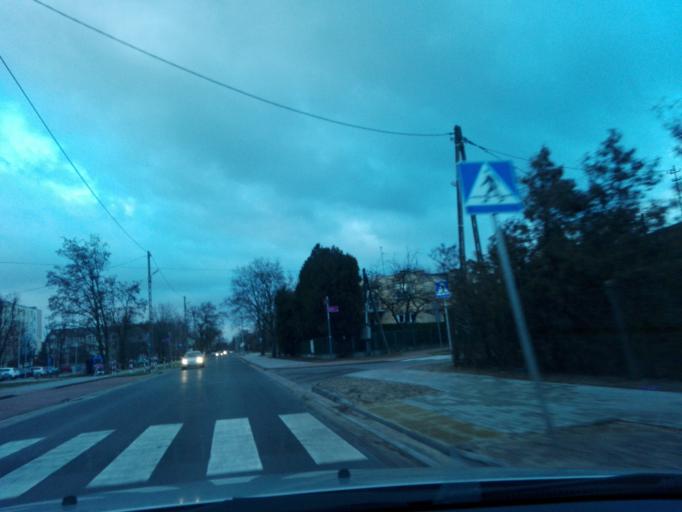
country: PL
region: Lodz Voivodeship
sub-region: Powiat kutnowski
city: Kutno
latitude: 52.2426
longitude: 19.3525
